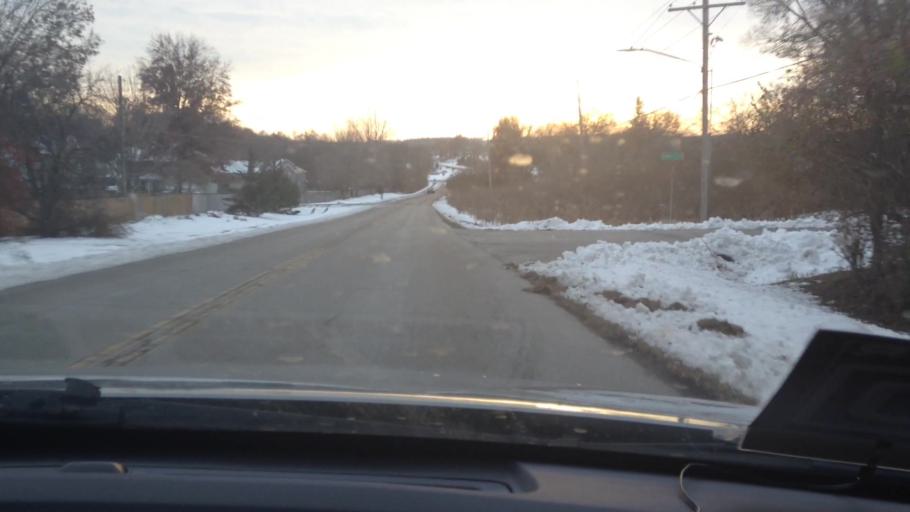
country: US
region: Kansas
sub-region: Leavenworth County
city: Leavenworth
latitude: 39.2850
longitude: -94.9446
